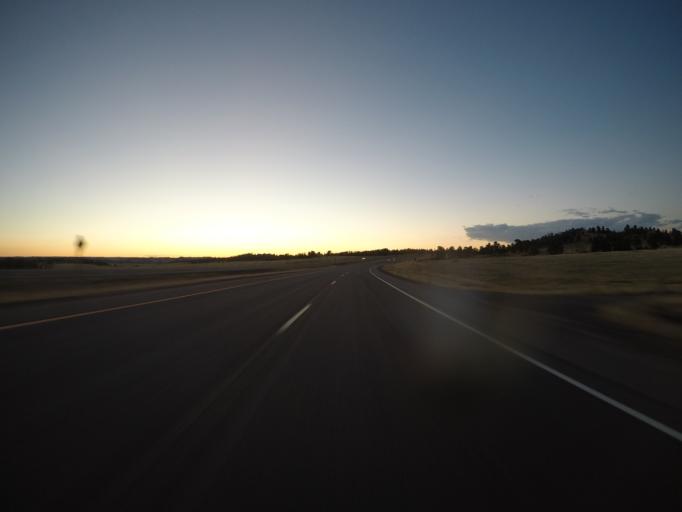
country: US
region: Wyoming
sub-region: Albany County
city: Laramie
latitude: 41.0057
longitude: -105.4175
